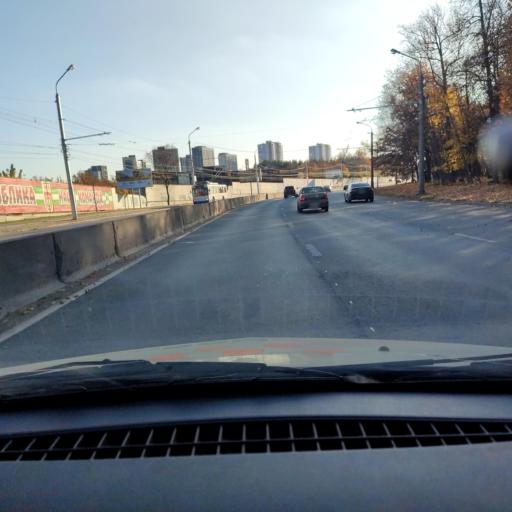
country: RU
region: Bashkortostan
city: Ufa
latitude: 54.7295
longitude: 56.0236
